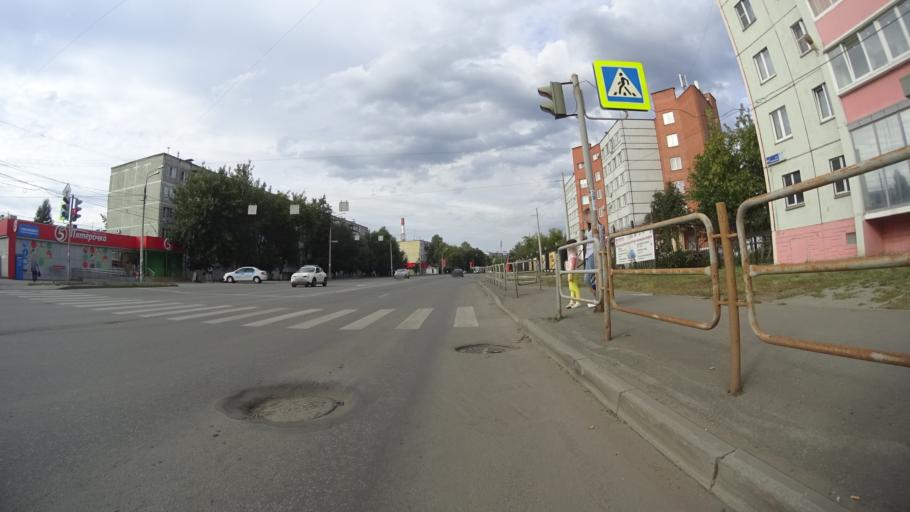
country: RU
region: Chelyabinsk
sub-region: Gorod Chelyabinsk
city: Chelyabinsk
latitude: 55.1988
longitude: 61.3185
